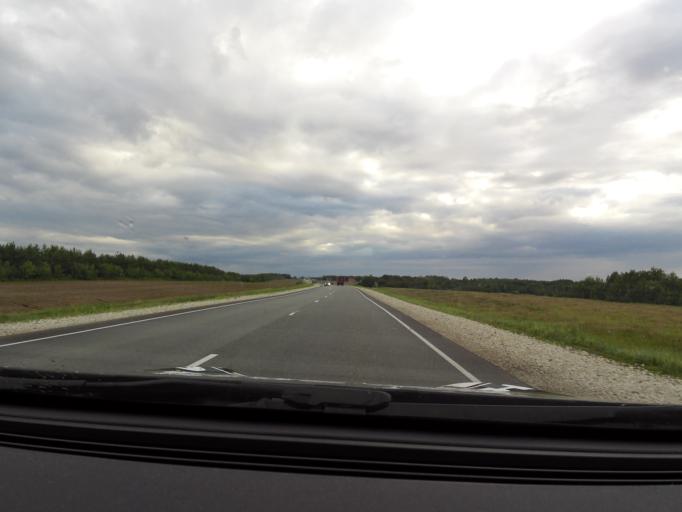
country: RU
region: Mariy-El
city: Volzhsk
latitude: 55.7282
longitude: 48.3976
